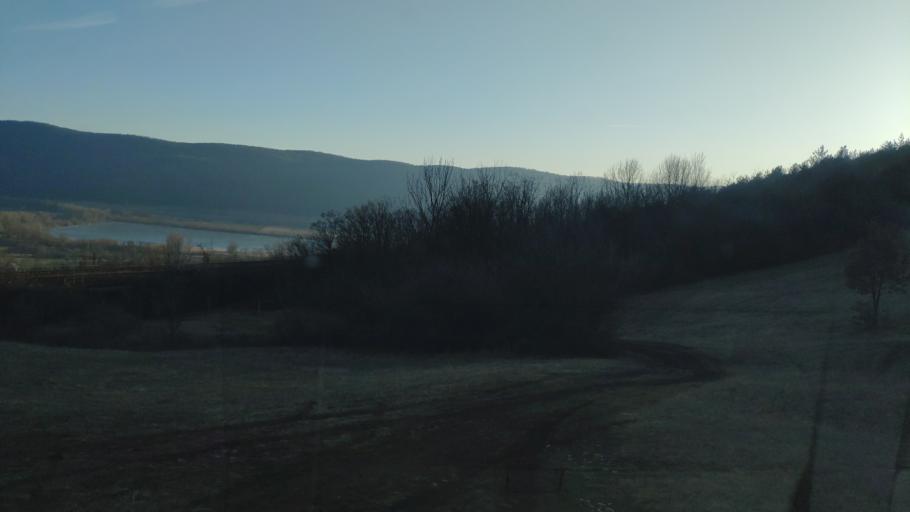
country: SK
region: Kosicky
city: Medzev
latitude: 48.6105
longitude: 20.7425
